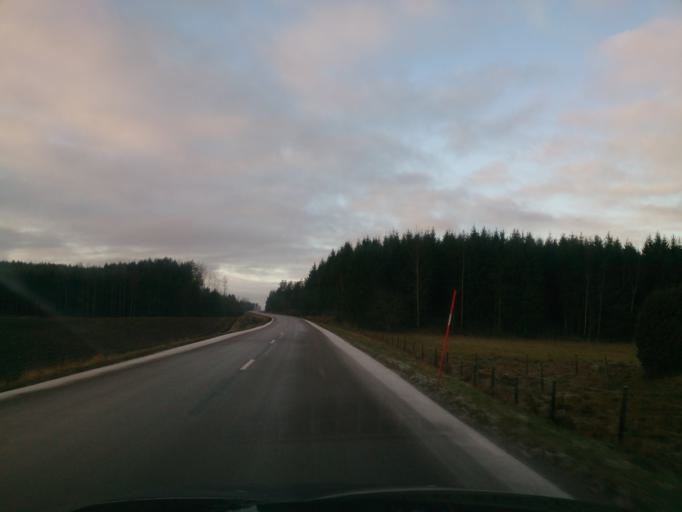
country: SE
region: OEstergoetland
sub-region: Linkopings Kommun
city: Linghem
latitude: 58.4124
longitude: 15.8977
